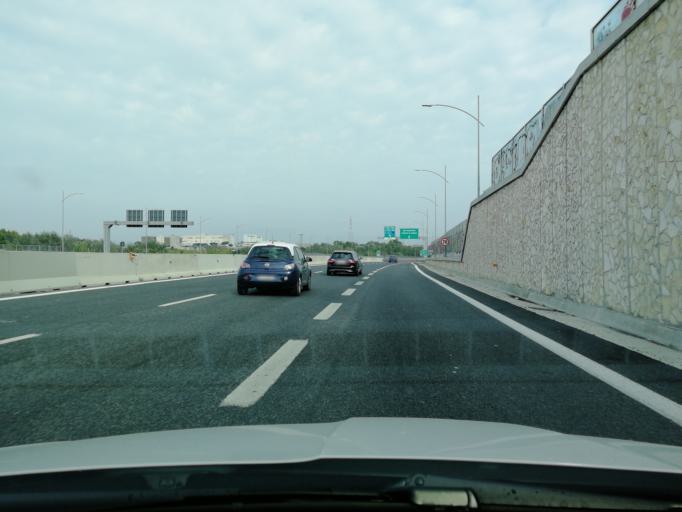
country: IT
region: Latium
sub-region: Citta metropolitana di Roma Capitale
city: Setteville
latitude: 41.9221
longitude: 12.6145
